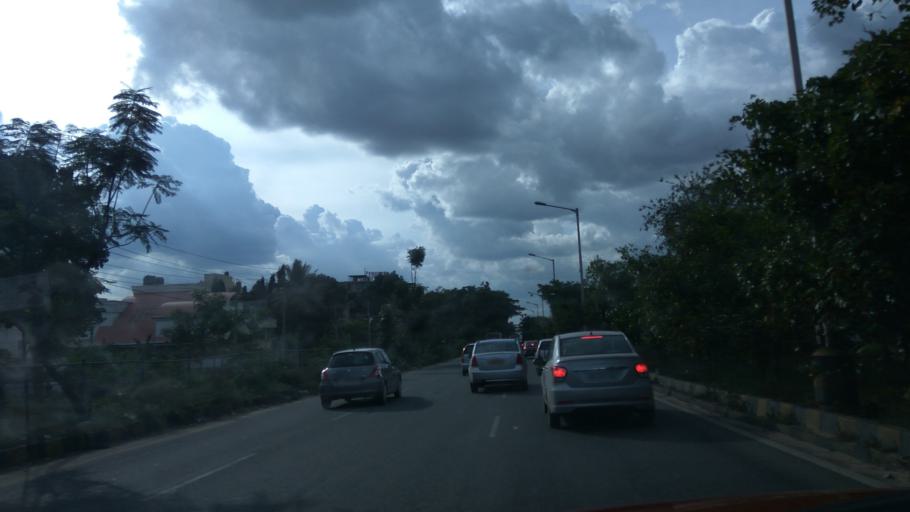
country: IN
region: Karnataka
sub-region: Bangalore Urban
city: Bangalore
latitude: 13.0198
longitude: 77.6533
